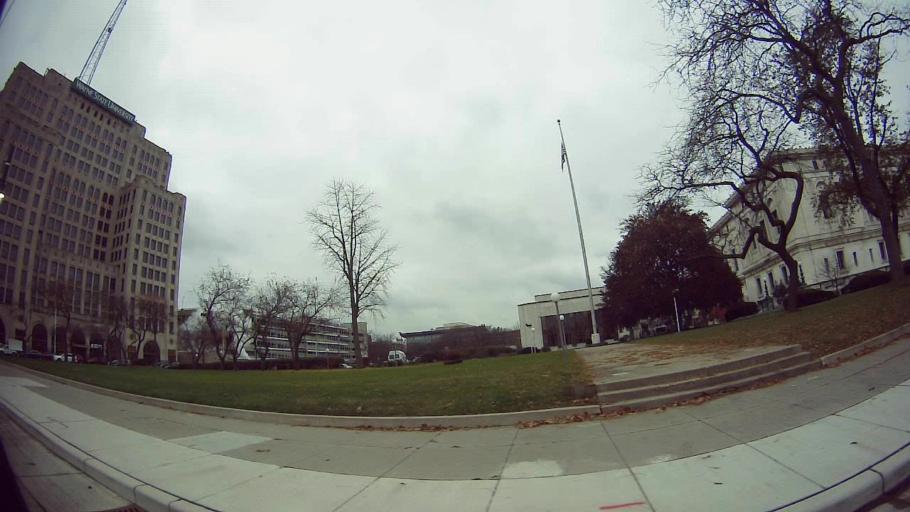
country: US
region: Michigan
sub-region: Wayne County
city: Detroit
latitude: 42.3584
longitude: -83.0655
